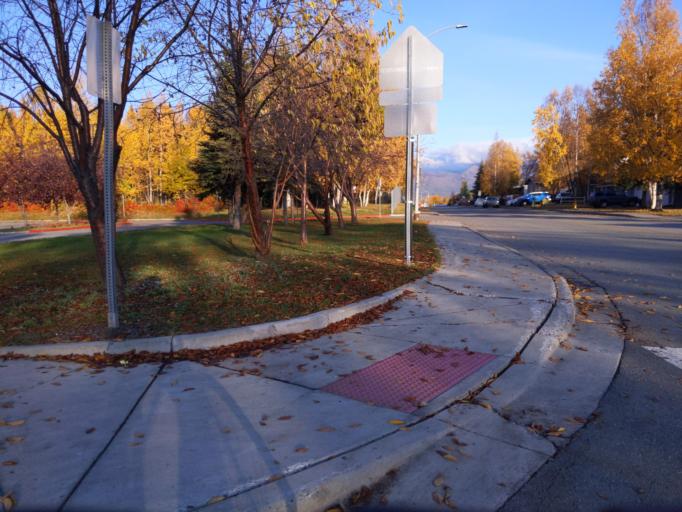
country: US
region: Alaska
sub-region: Anchorage Municipality
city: Anchorage
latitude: 61.1556
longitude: -149.8693
